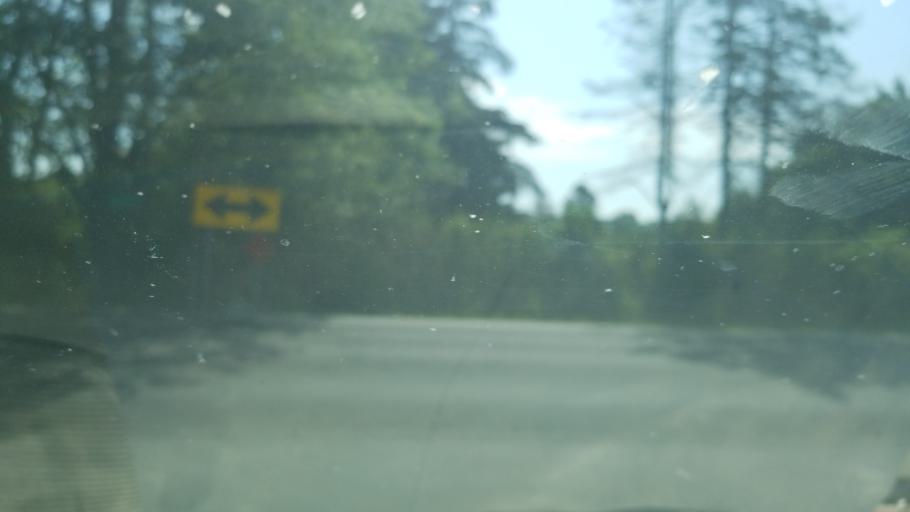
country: US
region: Ohio
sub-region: Delaware County
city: Sunbury
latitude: 40.2543
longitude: -82.9382
